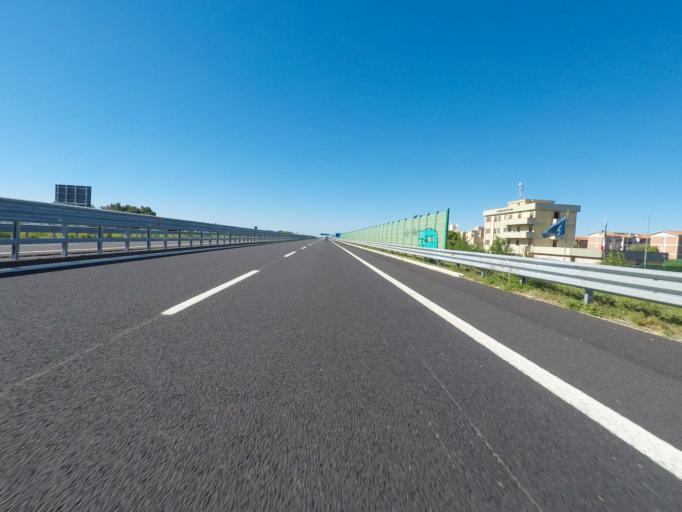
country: IT
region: Latium
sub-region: Provincia di Viterbo
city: Tarquinia
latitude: 42.2415
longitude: 11.7520
